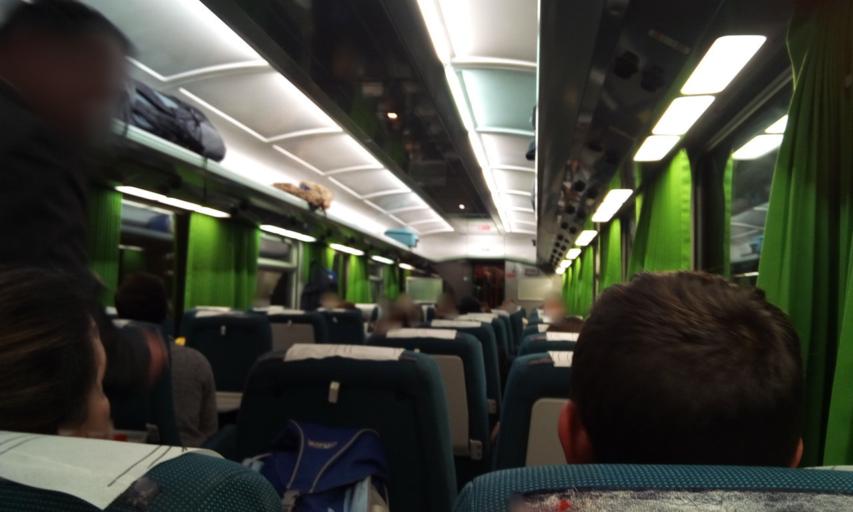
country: PT
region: Santarem
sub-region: Entroncamento
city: Entroncamento
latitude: 39.4670
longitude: -8.4681
